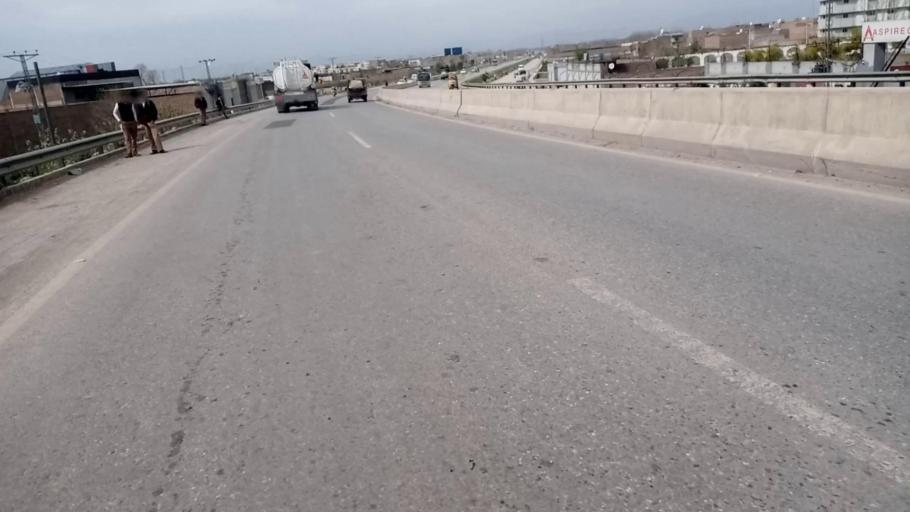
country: PK
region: Khyber Pakhtunkhwa
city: Peshawar
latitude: 34.0393
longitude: 71.6196
